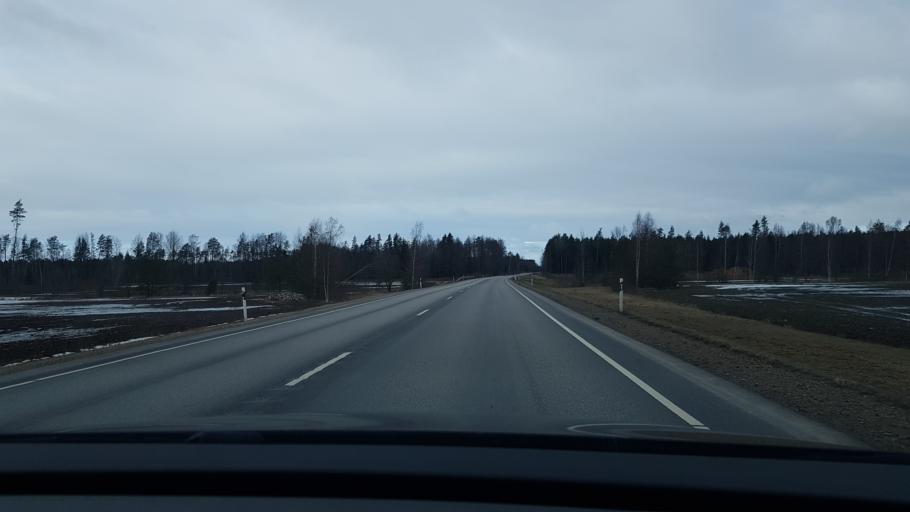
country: EE
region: Paernumaa
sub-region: Paikuse vald
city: Paikuse
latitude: 58.2753
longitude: 24.6251
